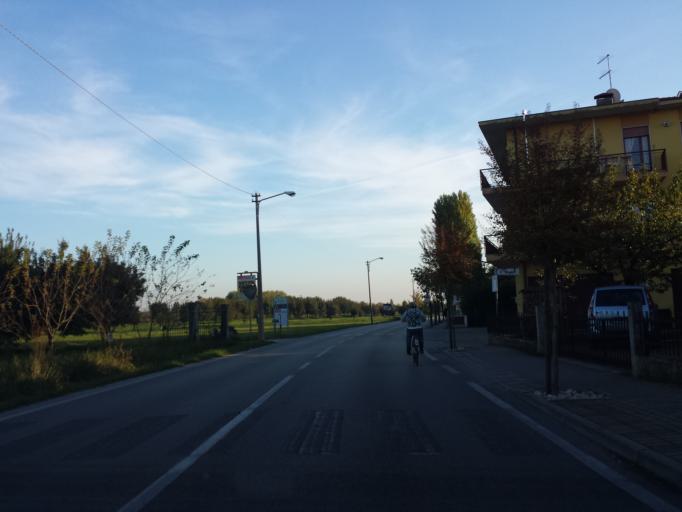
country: IT
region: Veneto
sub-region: Provincia di Vicenza
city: Crispi Cavour
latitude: 45.5859
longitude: 11.5328
